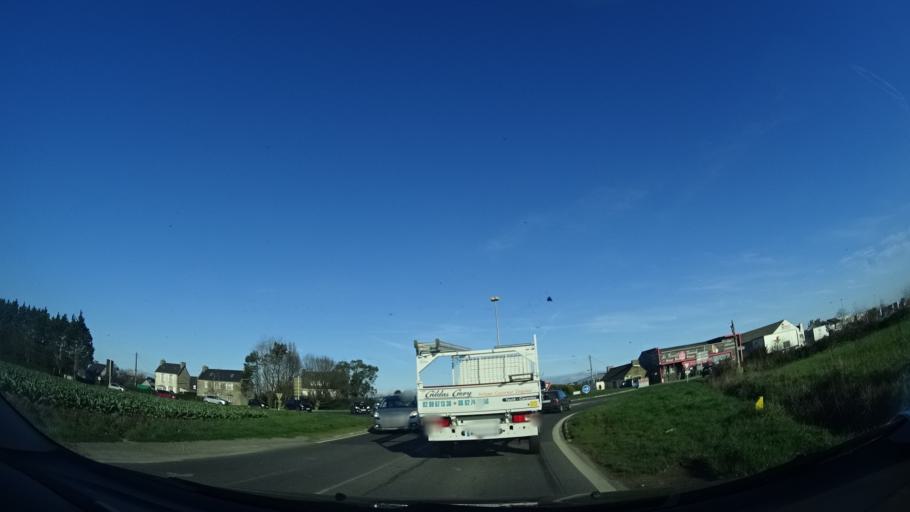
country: FR
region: Brittany
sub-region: Departement du Finistere
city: Saint-Pol-de-Leon
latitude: 48.6774
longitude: -4.0064
